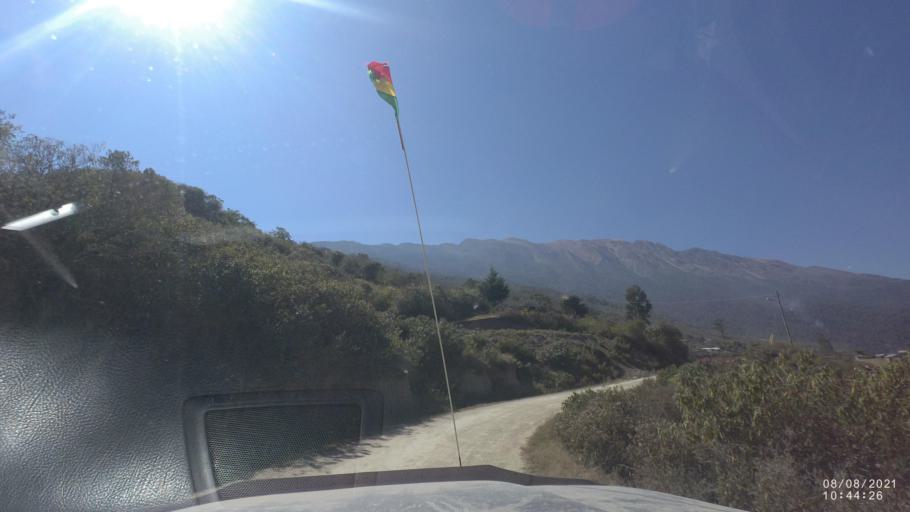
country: BO
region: La Paz
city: Quime
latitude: -16.7030
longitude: -66.7196
